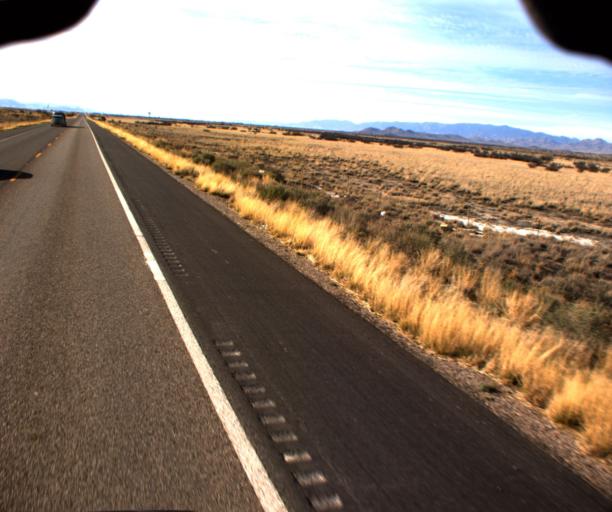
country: US
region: Arizona
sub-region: Cochise County
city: Willcox
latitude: 32.2182
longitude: -109.7869
